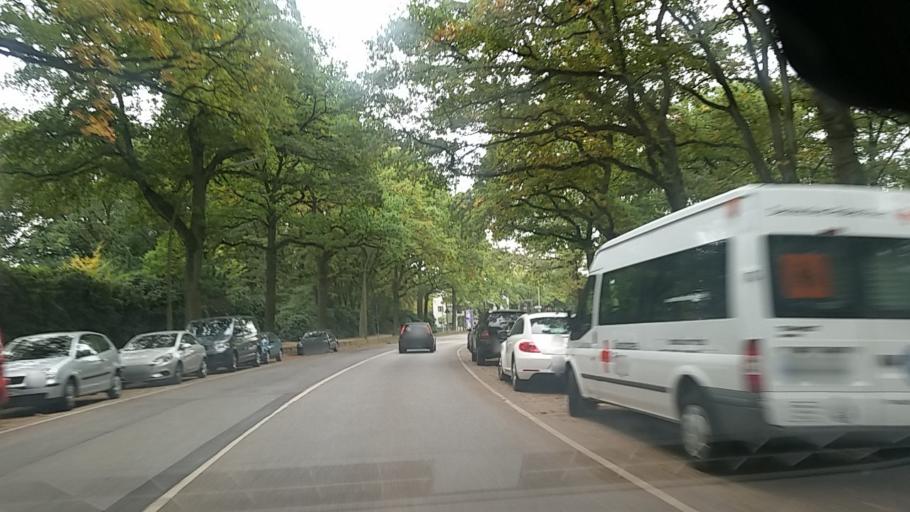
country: DE
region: Hamburg
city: Winterhude
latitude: 53.5932
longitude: 10.0149
